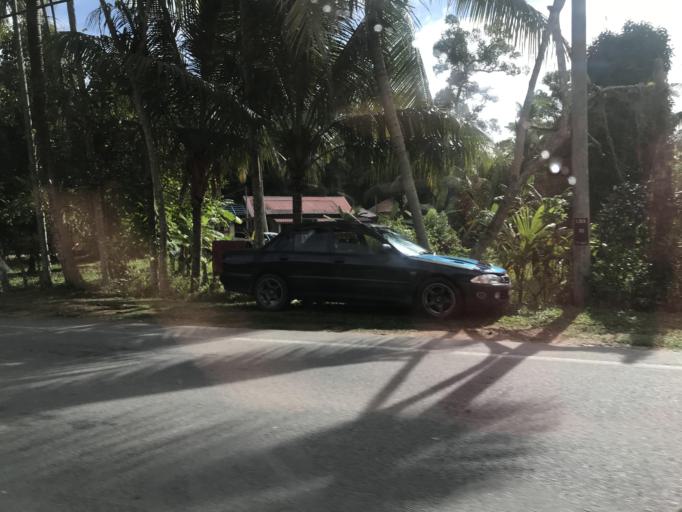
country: MY
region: Kelantan
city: Kota Bharu
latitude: 6.1221
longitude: 102.1756
